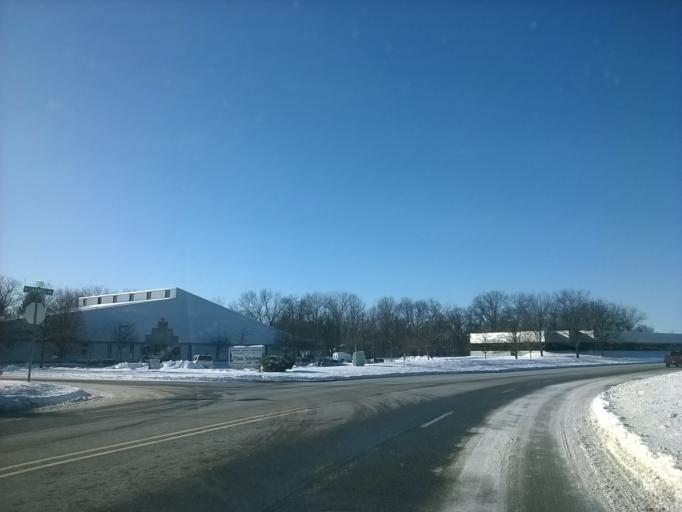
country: US
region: Indiana
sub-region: Hamilton County
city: Carmel
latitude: 39.9626
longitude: -86.1362
